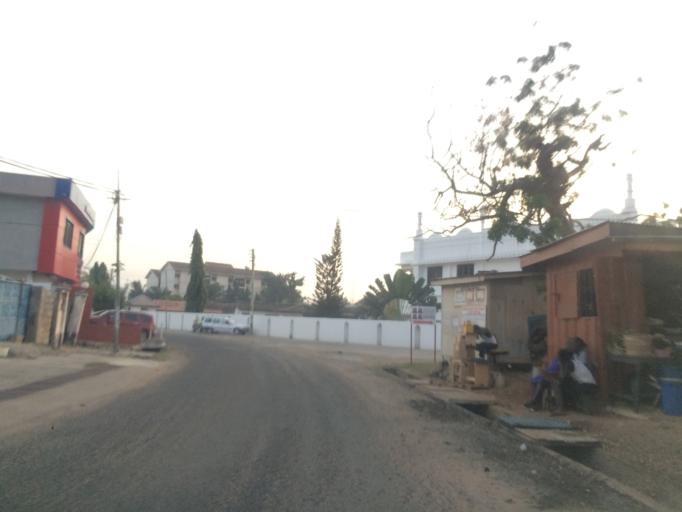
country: GH
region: Greater Accra
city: Accra
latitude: 5.5620
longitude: -0.1766
